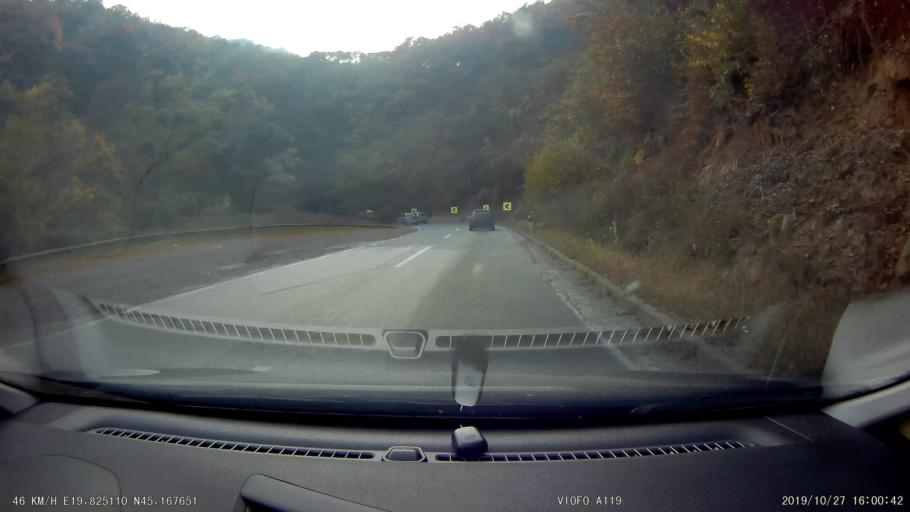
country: RS
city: Vrdnik
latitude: 45.1676
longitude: 19.8250
